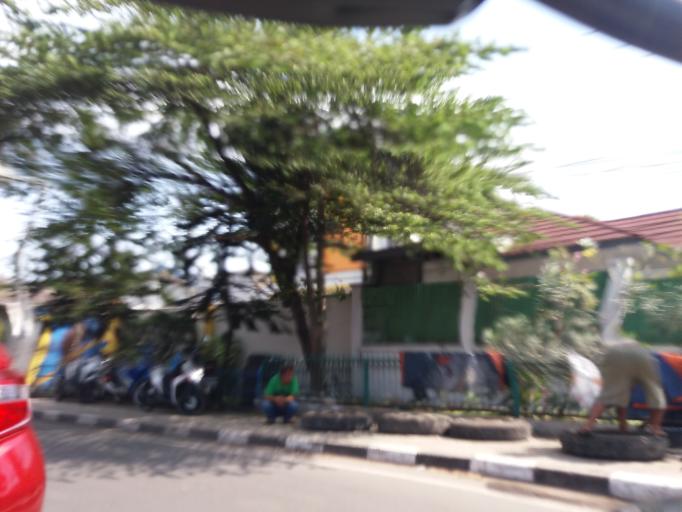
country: ID
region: West Java
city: Margahayukencana
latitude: -6.9332
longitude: 107.5718
